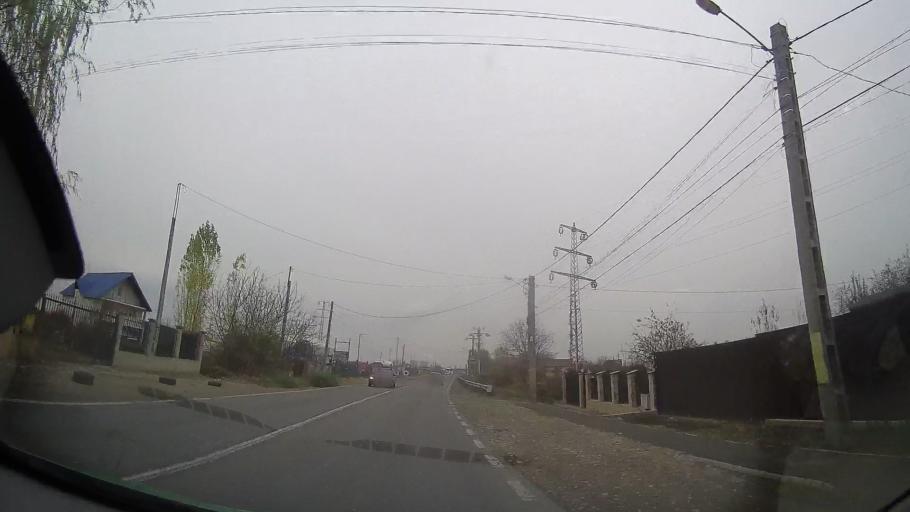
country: RO
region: Prahova
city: Ploiesti
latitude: 44.9624
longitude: 26.0399
